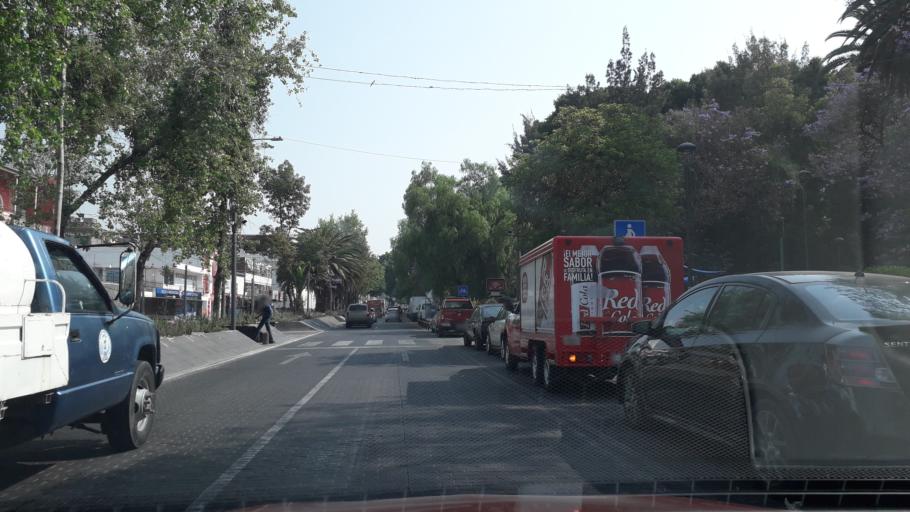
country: MX
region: Puebla
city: Puebla
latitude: 19.0470
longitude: -98.2083
